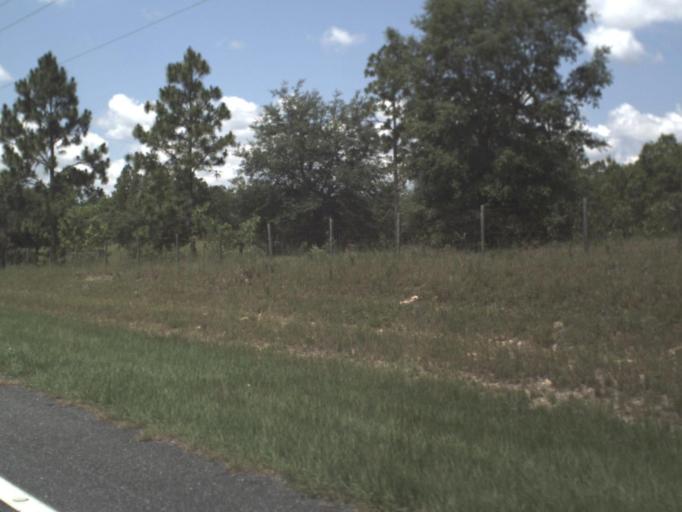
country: US
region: Florida
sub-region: Levy County
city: Williston Highlands
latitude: 29.2341
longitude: -82.5602
